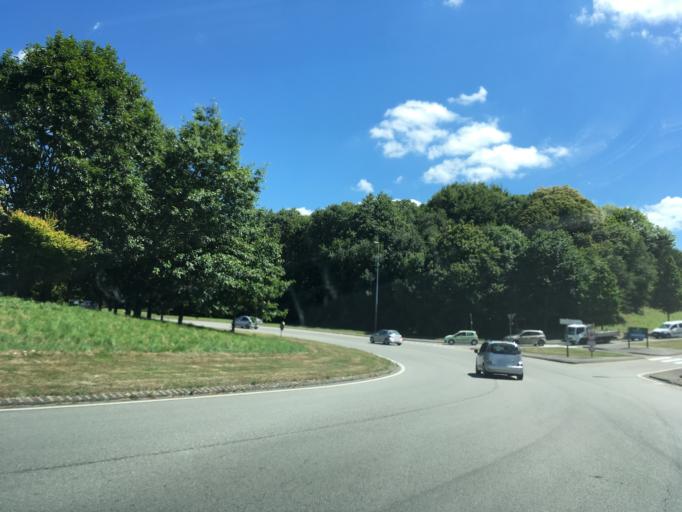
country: FR
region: Brittany
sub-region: Departement du Finistere
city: Quimper
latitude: 47.9799
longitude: -4.0806
